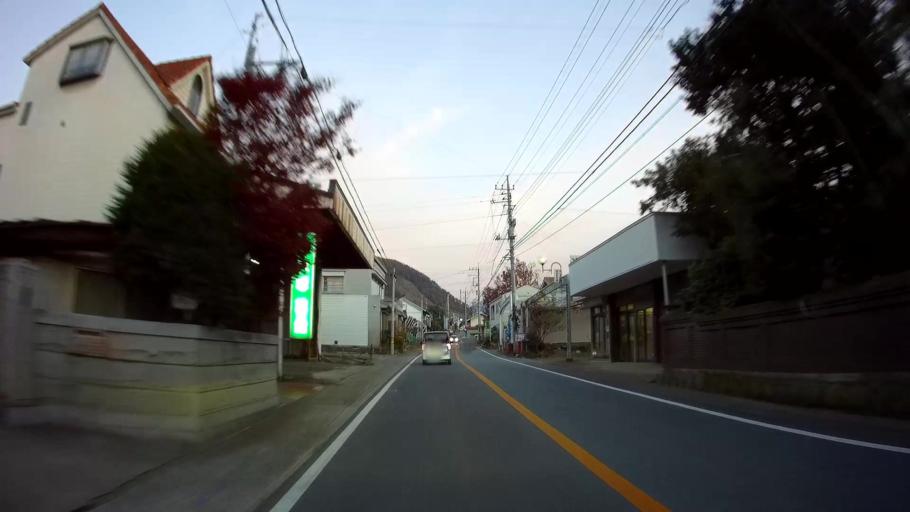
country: JP
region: Yamanashi
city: Enzan
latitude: 35.6633
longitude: 138.7257
